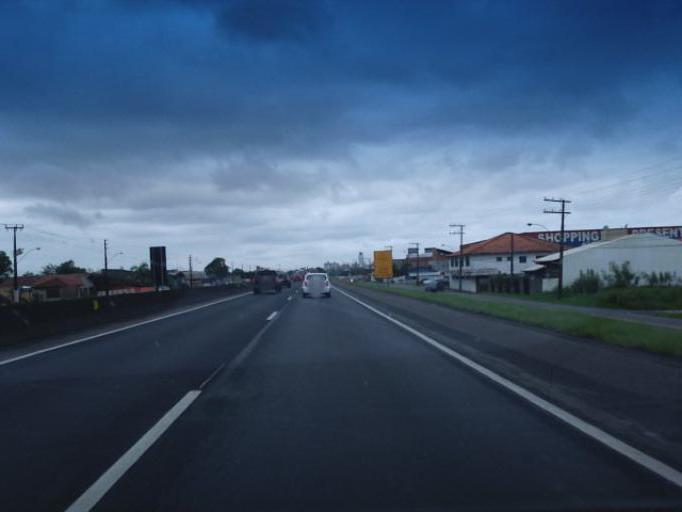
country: BR
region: Santa Catarina
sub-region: Barra Velha
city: Barra Velha
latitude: -26.6562
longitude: -48.6878
